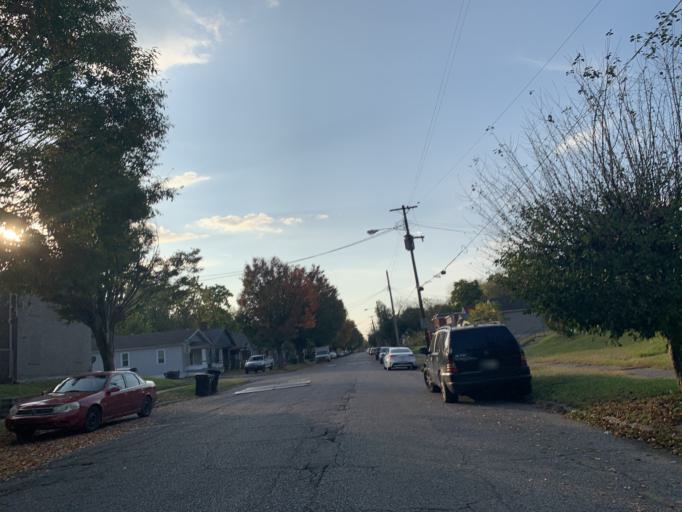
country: US
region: Kentucky
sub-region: Jefferson County
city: Louisville
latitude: 38.2350
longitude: -85.7835
